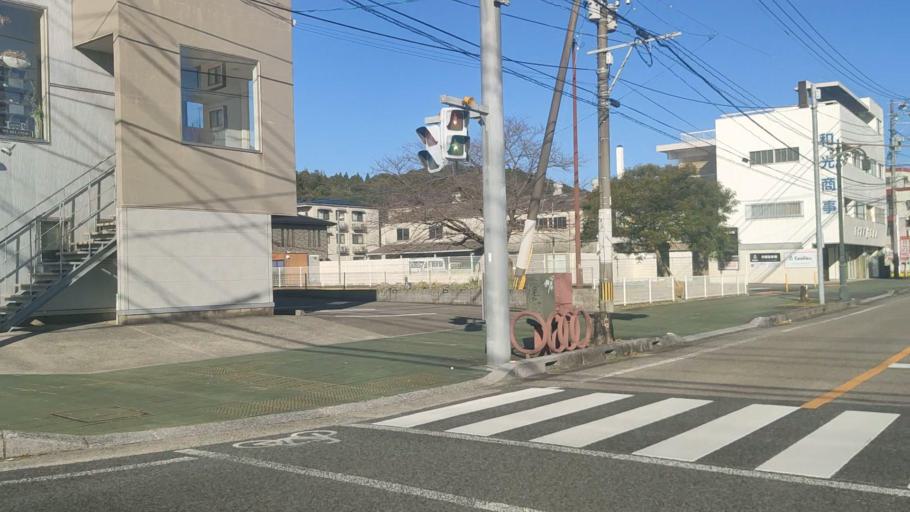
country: JP
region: Miyazaki
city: Nobeoka
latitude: 32.5853
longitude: 131.6713
